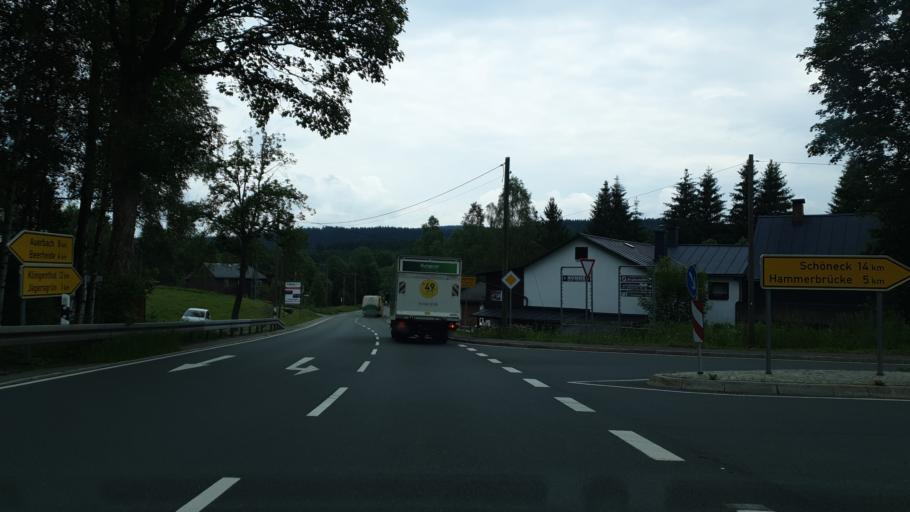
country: DE
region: Saxony
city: Tannenbergsthal
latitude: 50.4533
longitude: 12.4641
